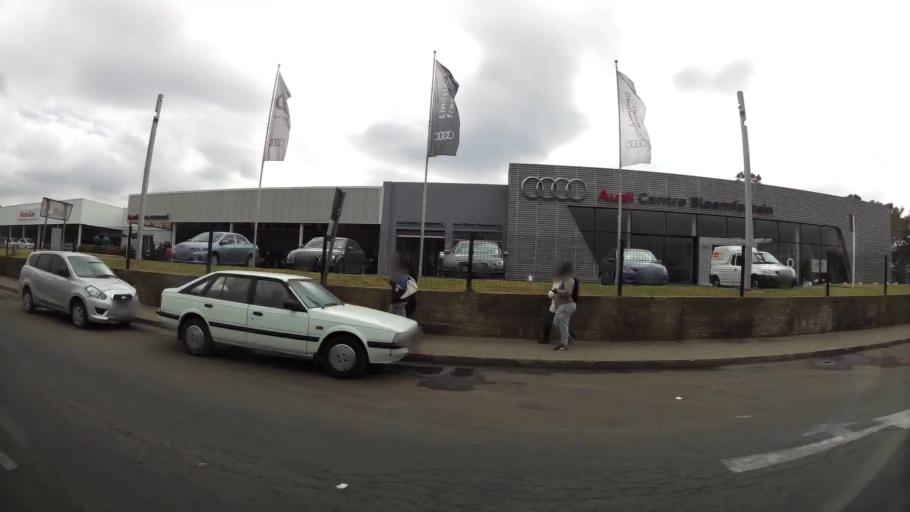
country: ZA
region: Orange Free State
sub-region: Mangaung Metropolitan Municipality
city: Bloemfontein
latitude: -29.1131
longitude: 26.2210
